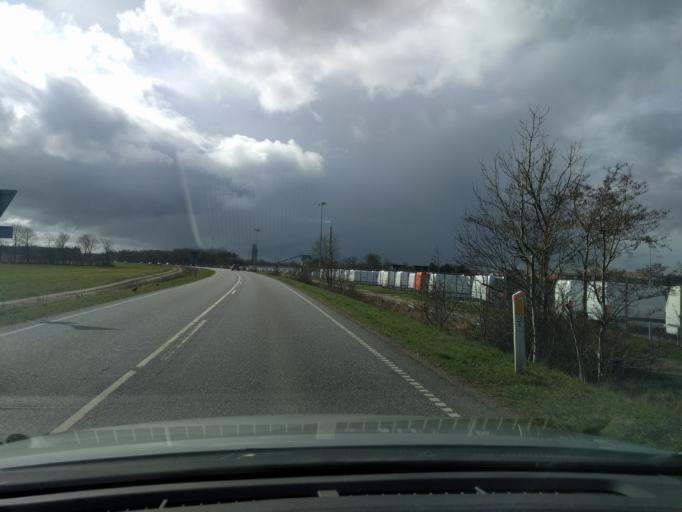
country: DK
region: South Denmark
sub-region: Kolding Kommune
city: Vamdrup
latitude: 55.4348
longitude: 9.3157
